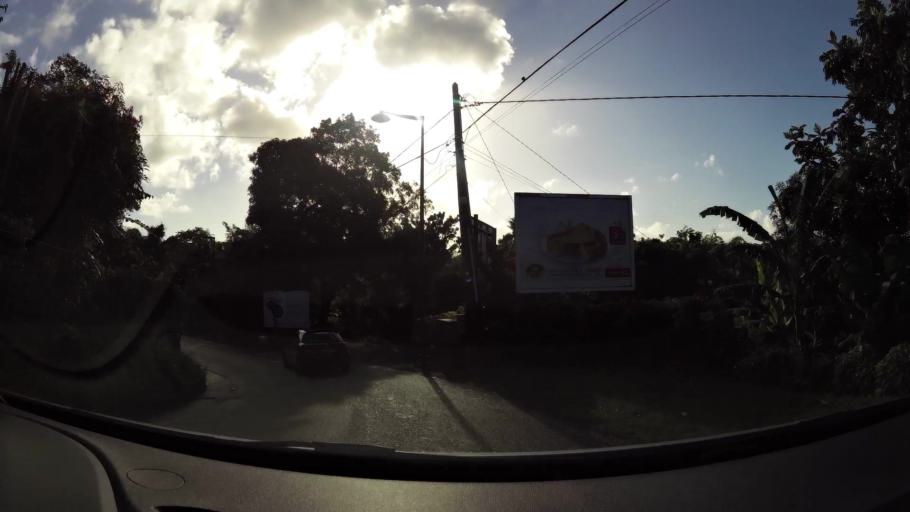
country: MQ
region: Martinique
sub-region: Martinique
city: Le Lamentin
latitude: 14.6221
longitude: -61.0241
